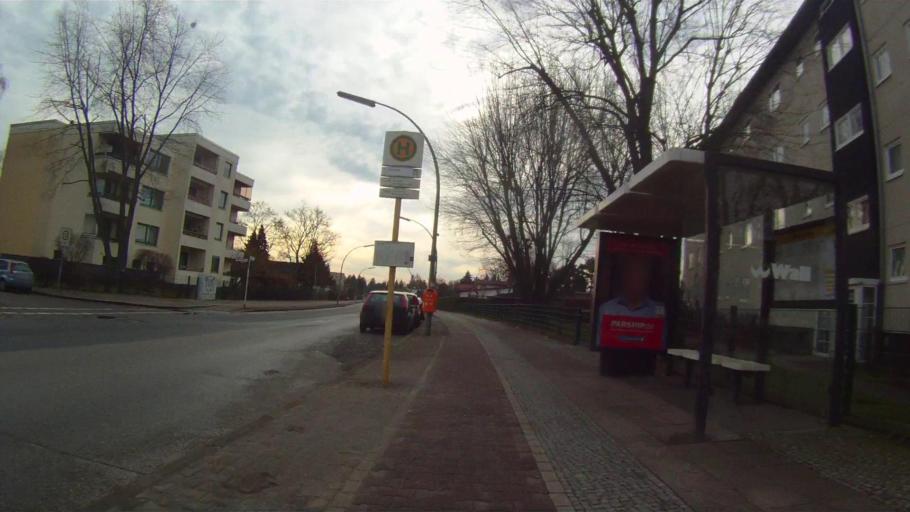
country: DE
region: Berlin
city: Lichtenrade
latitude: 52.4210
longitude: 13.4151
